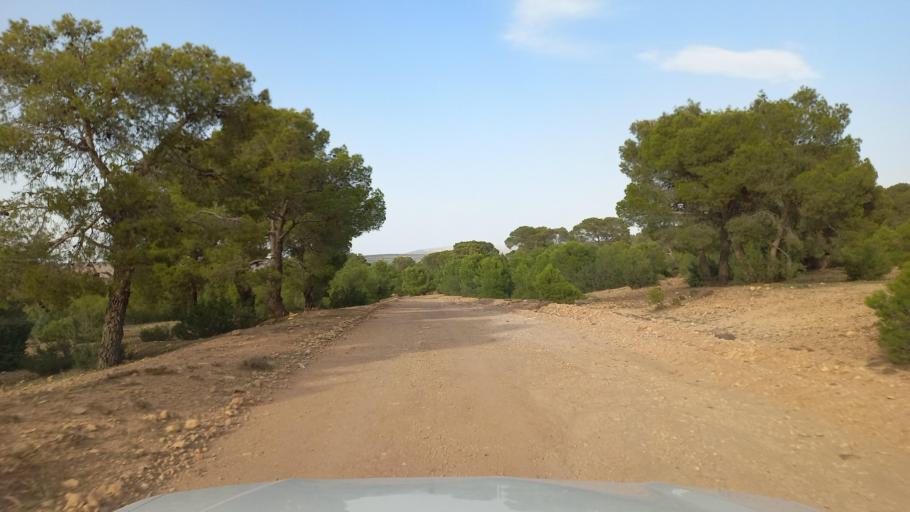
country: TN
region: Al Qasrayn
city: Kasserine
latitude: 35.3367
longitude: 8.8546
